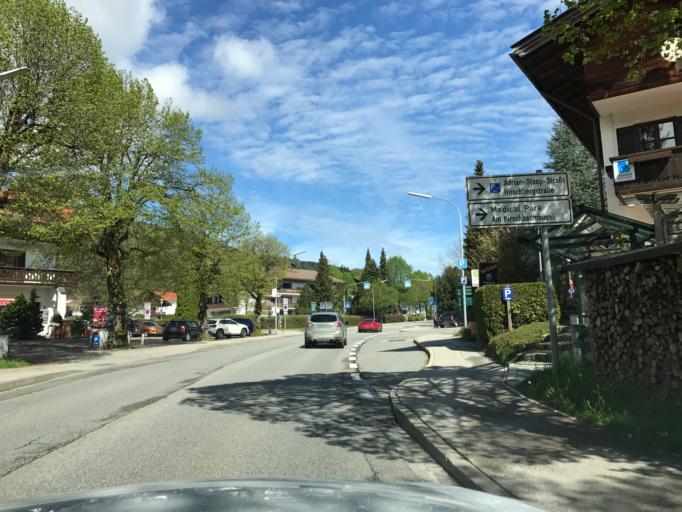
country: DE
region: Bavaria
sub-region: Upper Bavaria
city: Bad Wiessee
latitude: 47.7161
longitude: 11.7204
